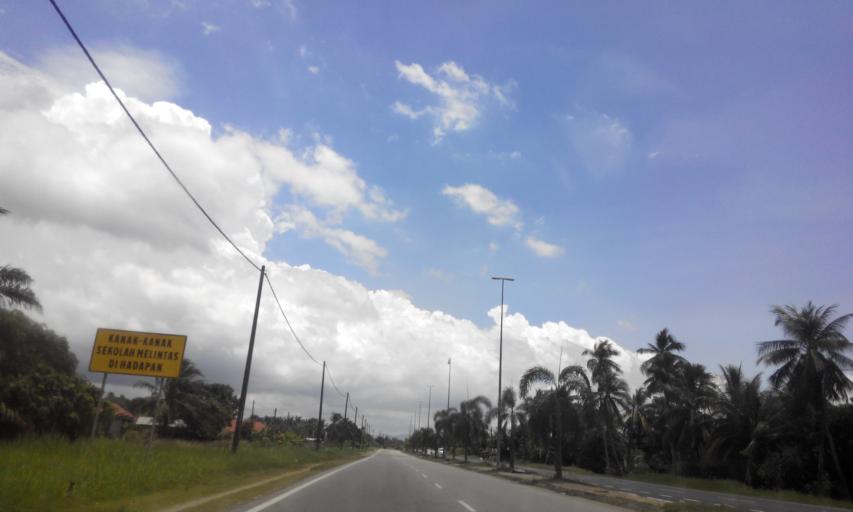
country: MY
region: Perak
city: Parit Buntar
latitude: 5.1231
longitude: 100.5173
